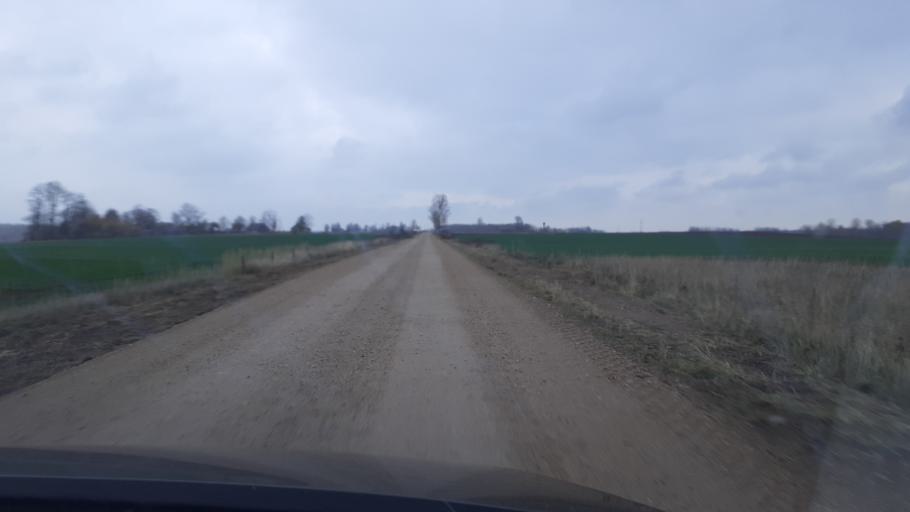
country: LV
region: Talsu Rajons
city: Sabile
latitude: 56.9330
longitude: 22.4171
